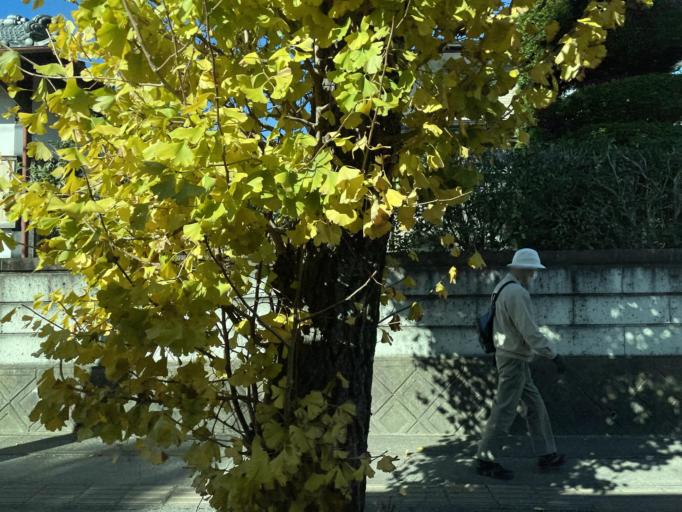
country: JP
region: Saitama
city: Kukichuo
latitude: 36.0645
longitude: 139.6892
